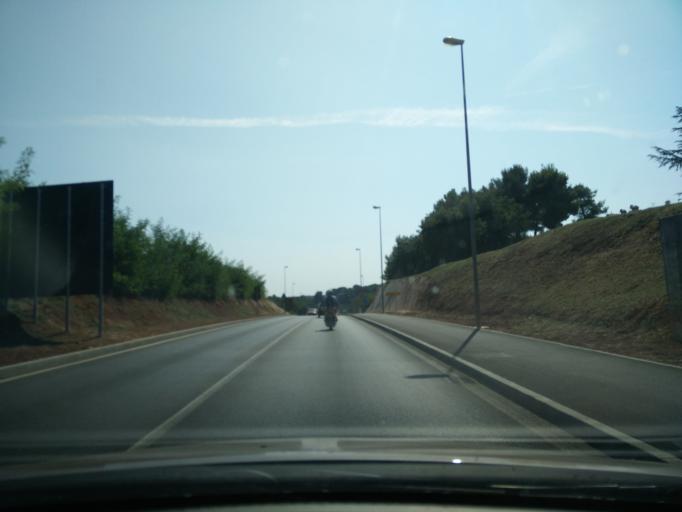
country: HR
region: Istarska
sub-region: Grad Porec
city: Porec
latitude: 45.2165
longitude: 13.6043
